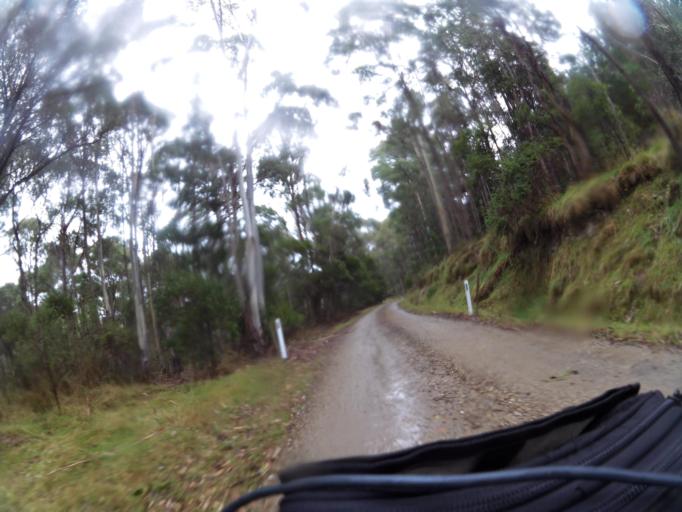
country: AU
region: New South Wales
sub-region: Greater Hume Shire
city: Holbrook
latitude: -36.1955
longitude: 147.5335
